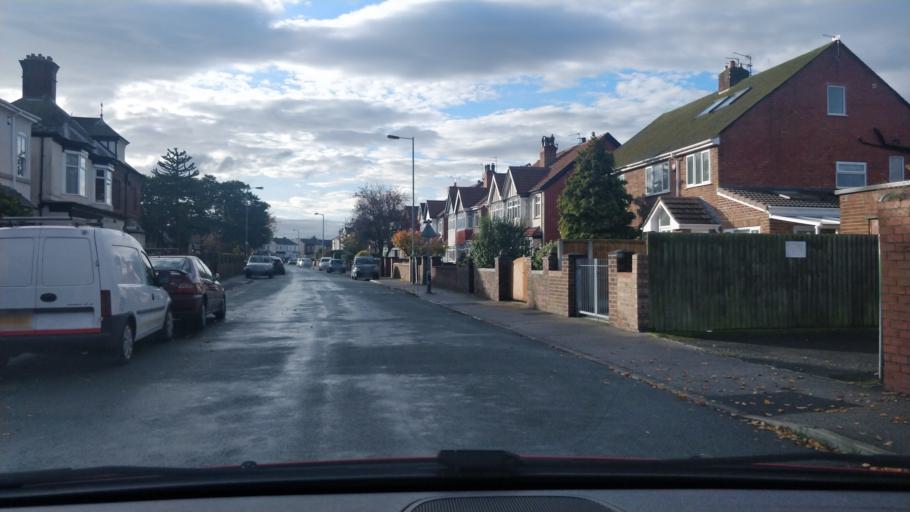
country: GB
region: England
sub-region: Sefton
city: Southport
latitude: 53.6348
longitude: -3.0076
